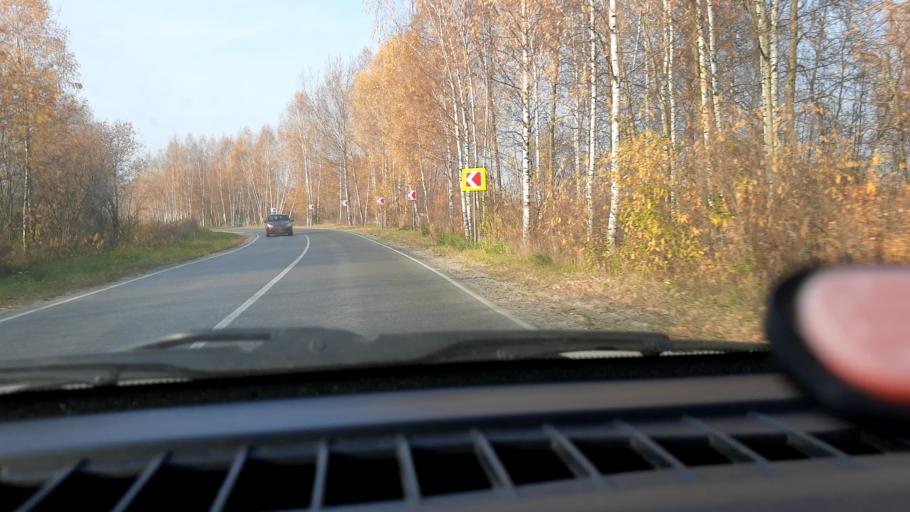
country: RU
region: Nizjnij Novgorod
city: Neklyudovo
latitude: 56.4639
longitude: 43.8996
